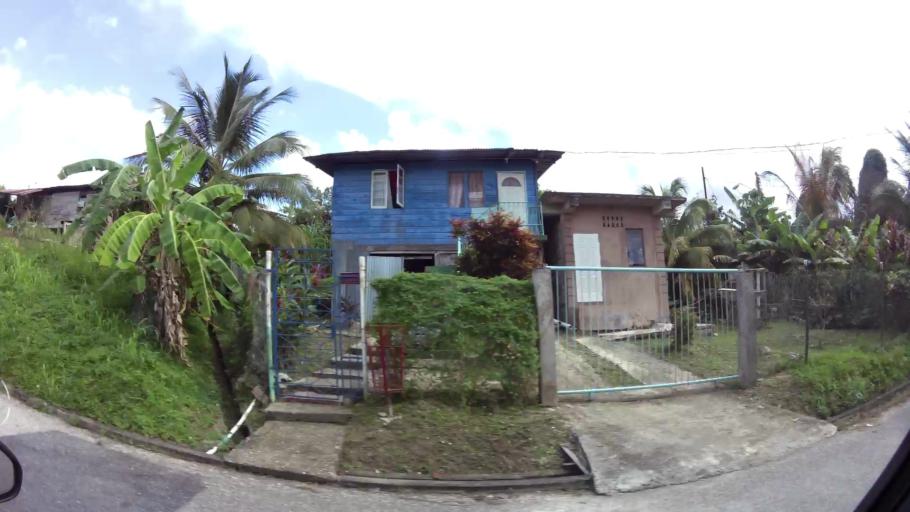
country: TT
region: City of San Fernando
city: Mon Repos
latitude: 10.2763
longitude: -61.4478
